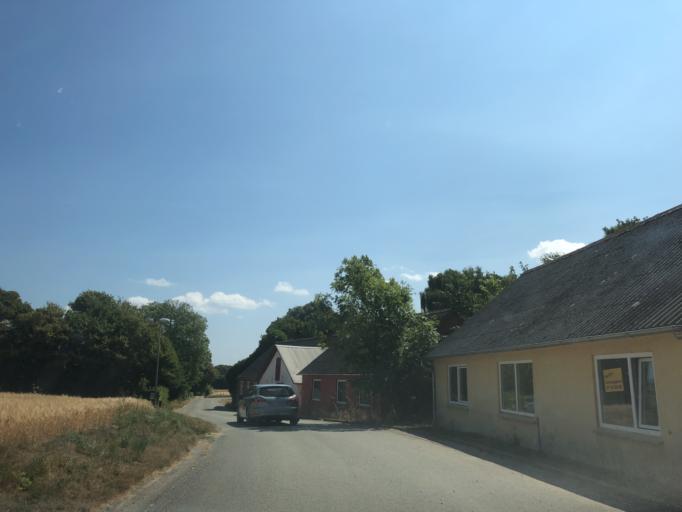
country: DK
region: North Denmark
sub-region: Morso Kommune
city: Nykobing Mors
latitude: 56.8252
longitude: 8.9950
